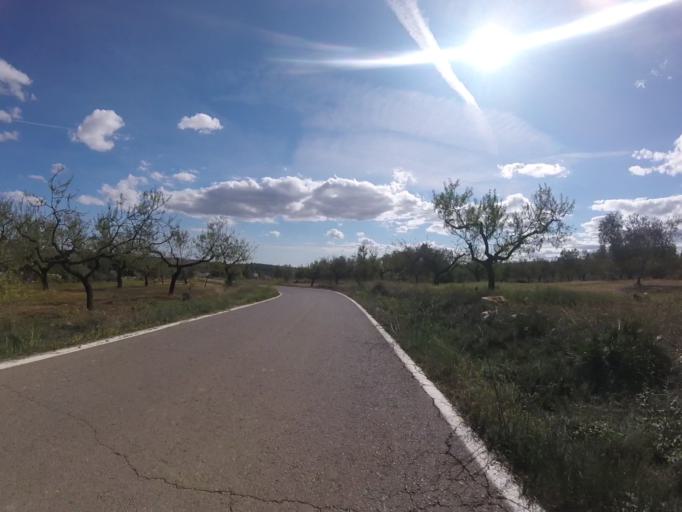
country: ES
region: Valencia
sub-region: Provincia de Castello
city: Albocasser
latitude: 40.3995
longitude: 0.0861
